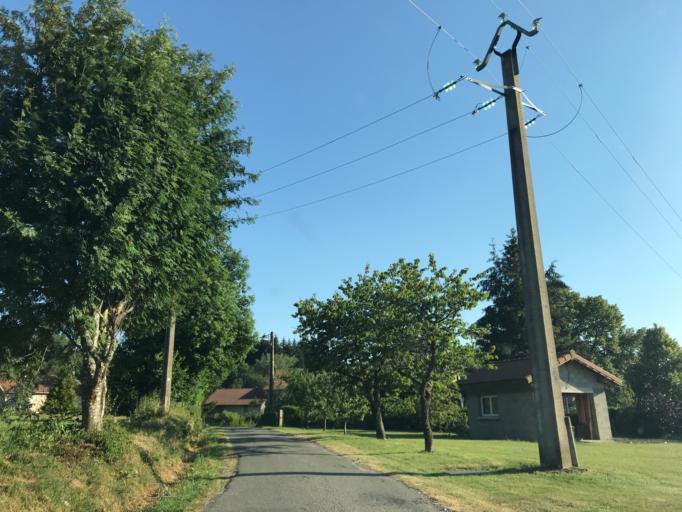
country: FR
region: Auvergne
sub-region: Departement du Puy-de-Dome
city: Celles-sur-Durolle
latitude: 45.7871
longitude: 3.6829
